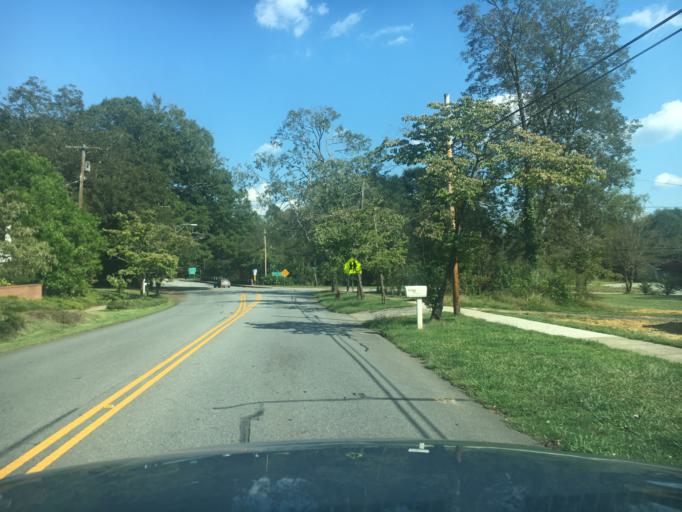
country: US
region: South Carolina
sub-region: Anderson County
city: Pendleton
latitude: 34.6513
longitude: -82.7802
